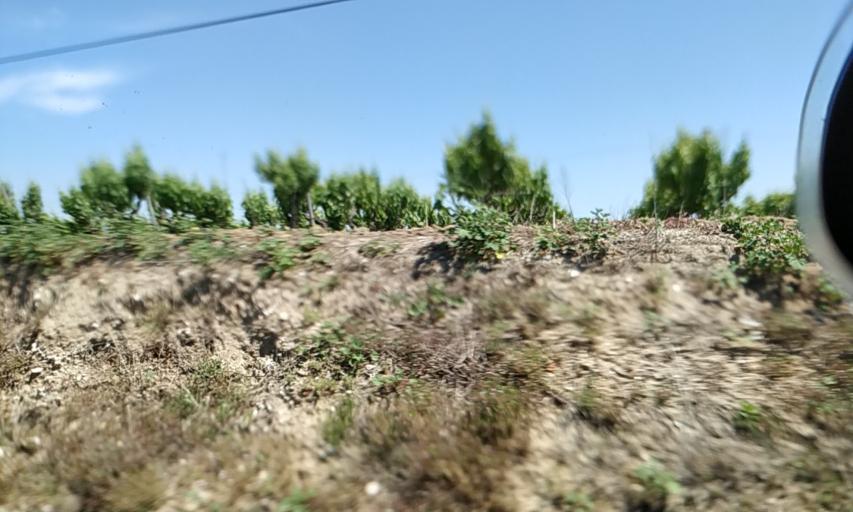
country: PT
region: Santarem
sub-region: Benavente
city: Poceirao
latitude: 38.6639
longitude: -8.7380
